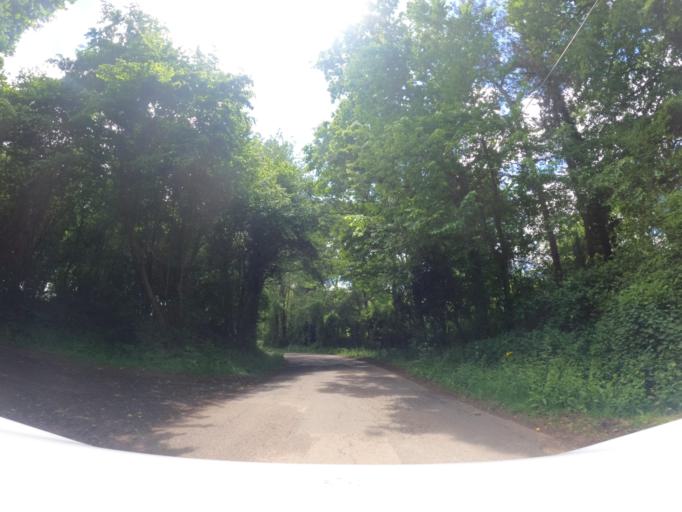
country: FR
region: Pays de la Loire
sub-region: Departement de la Vendee
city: Le Champ-Saint-Pere
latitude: 46.4978
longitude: -1.3515
